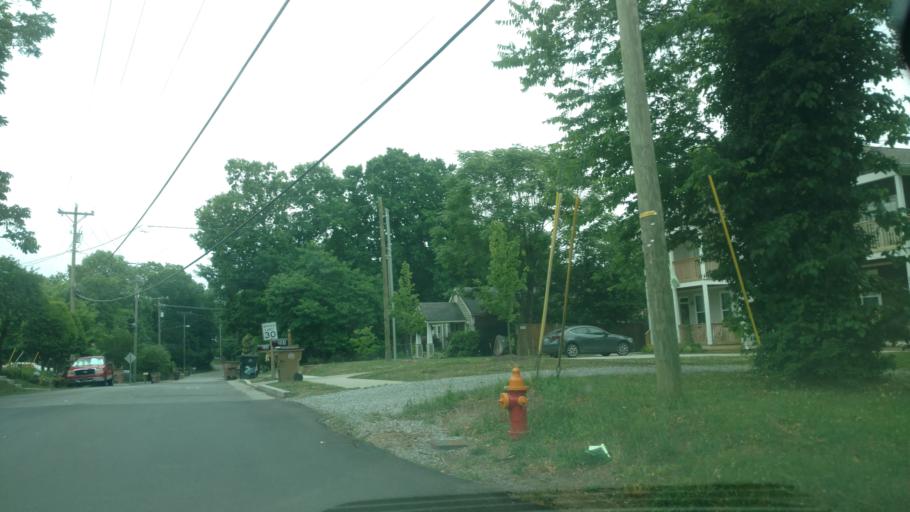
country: US
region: Tennessee
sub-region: Davidson County
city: Nashville
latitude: 36.1929
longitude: -86.7239
